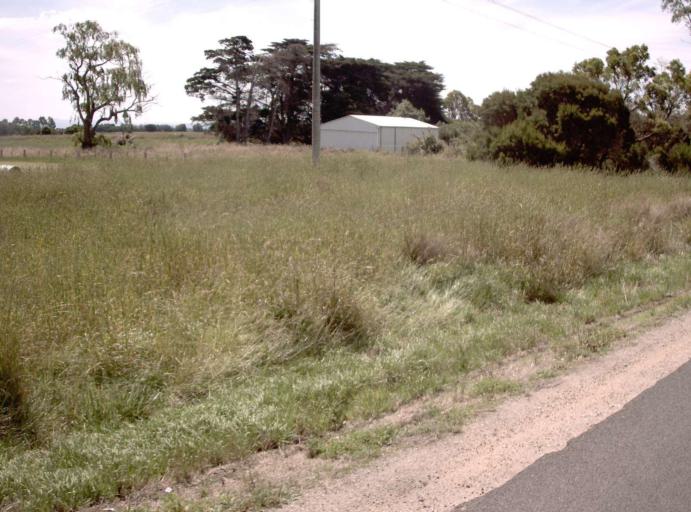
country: AU
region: Victoria
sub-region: Wellington
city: Sale
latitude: -38.0756
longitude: 147.0724
